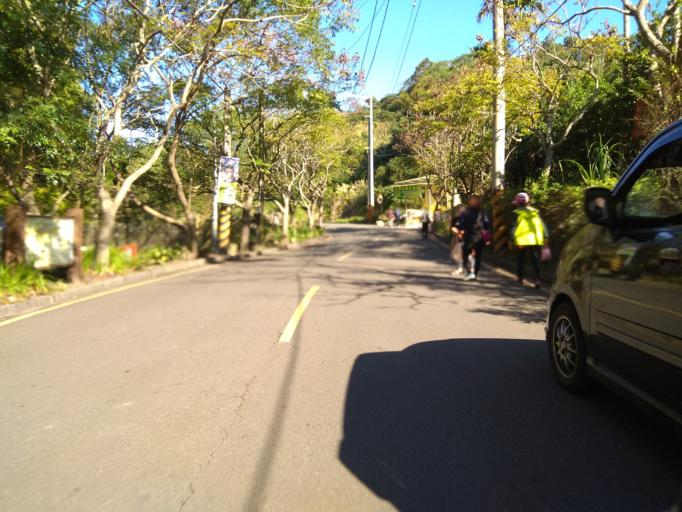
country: TW
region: Taiwan
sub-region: Hsinchu
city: Zhubei
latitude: 24.8586
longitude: 121.1053
